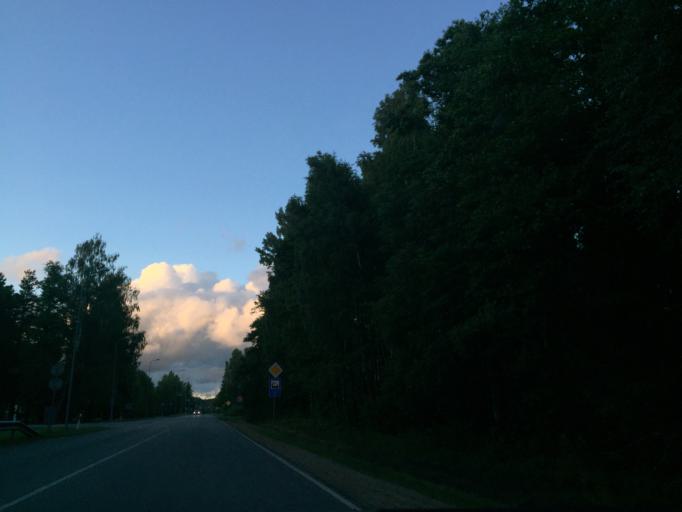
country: LV
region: Saulkrastu
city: Saulkrasti
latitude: 57.3130
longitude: 24.4144
